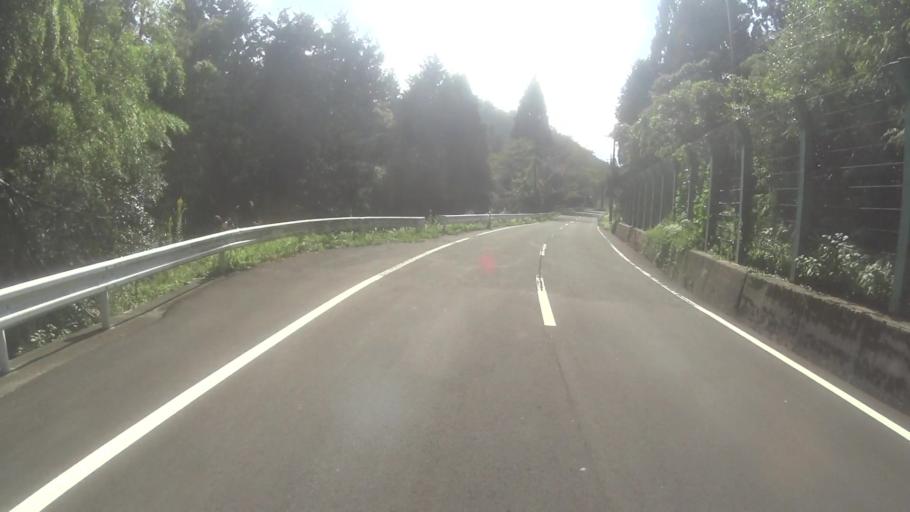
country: JP
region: Kyoto
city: Miyazu
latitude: 35.6894
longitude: 135.1173
